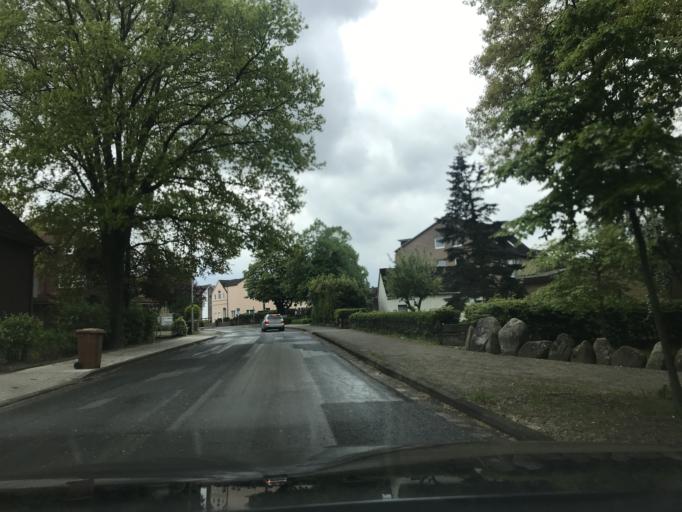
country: DE
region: Lower Saxony
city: Ganderkesee
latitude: 53.0297
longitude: 8.5440
